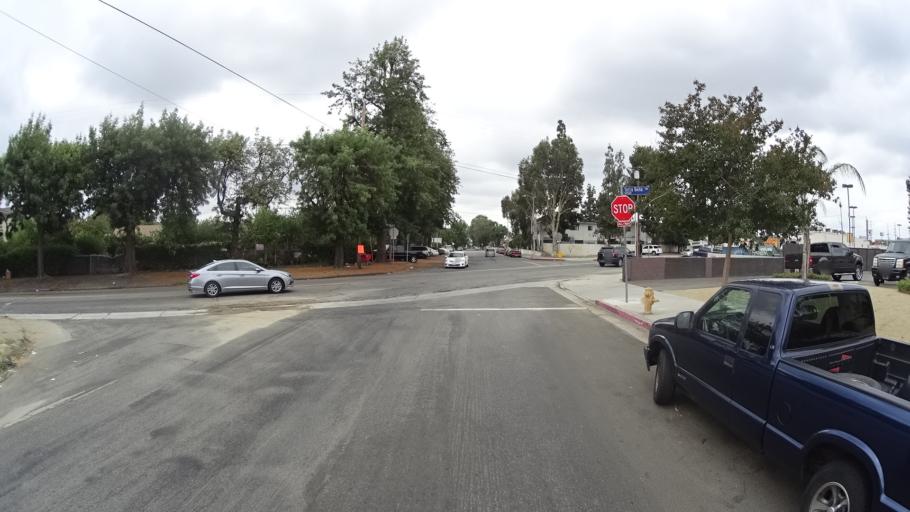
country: US
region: California
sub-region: Los Angeles County
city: San Fernando
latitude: 34.2368
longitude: -118.4481
